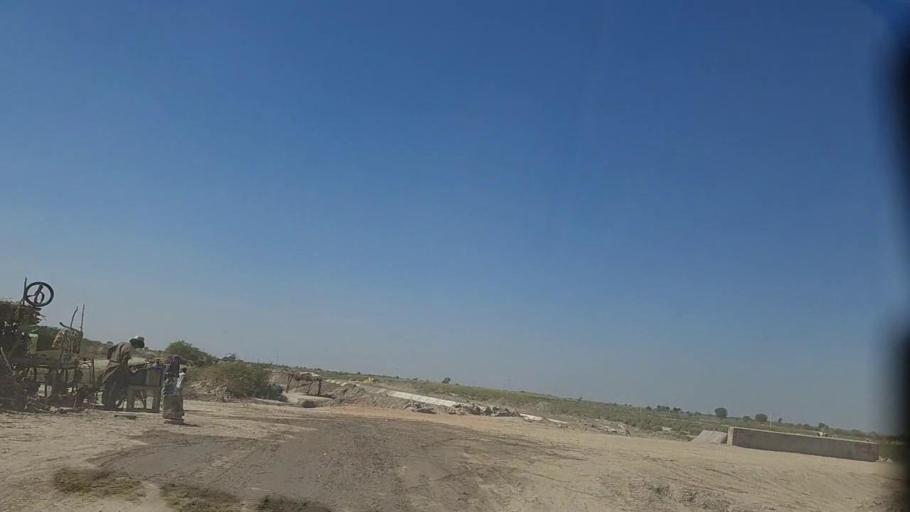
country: PK
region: Sindh
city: Mirwah Gorchani
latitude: 25.2266
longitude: 69.0181
